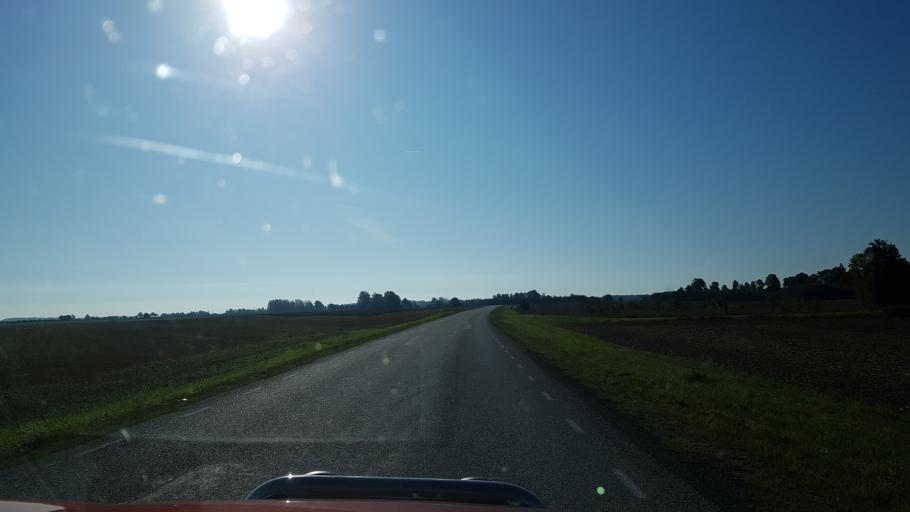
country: EE
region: Jogevamaa
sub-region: Tabivere vald
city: Tabivere
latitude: 58.6802
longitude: 26.6632
